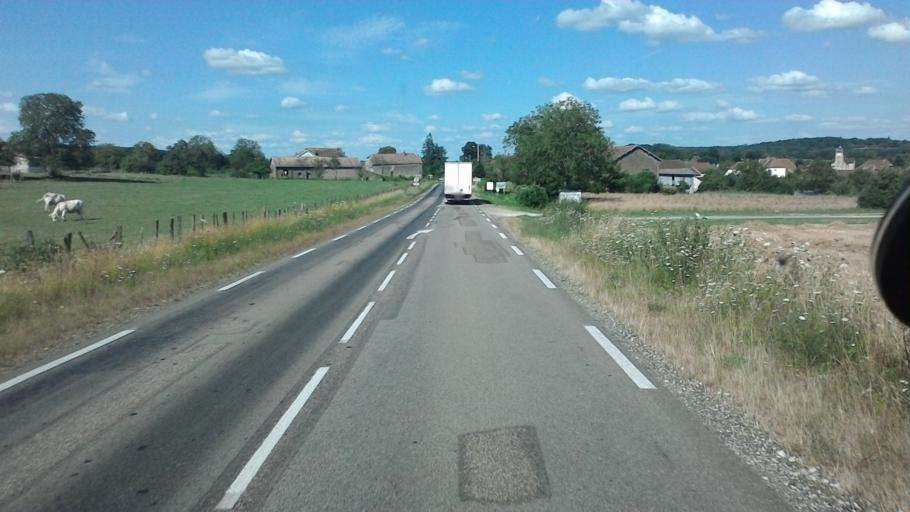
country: FR
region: Franche-Comte
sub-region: Departement de la Haute-Saone
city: Marnay
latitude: 47.3188
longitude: 5.6766
